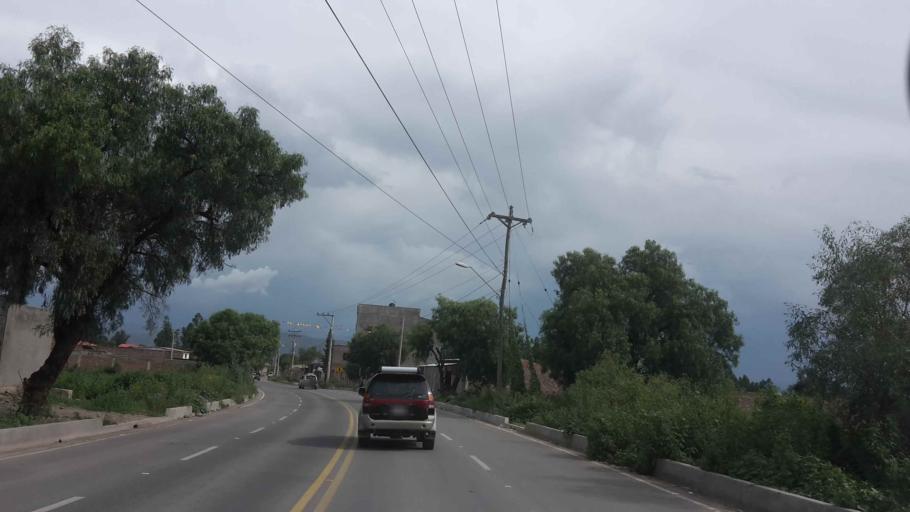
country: BO
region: Cochabamba
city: Cochabamba
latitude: -17.3550
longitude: -66.2546
